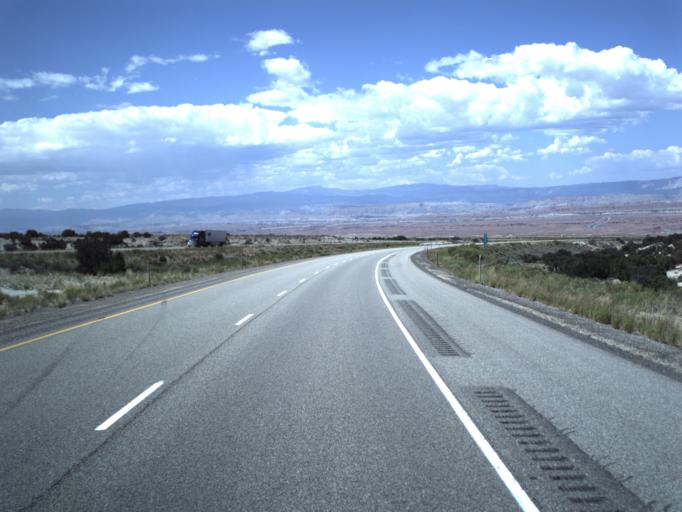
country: US
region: Utah
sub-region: Emery County
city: Ferron
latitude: 38.8422
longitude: -110.9547
